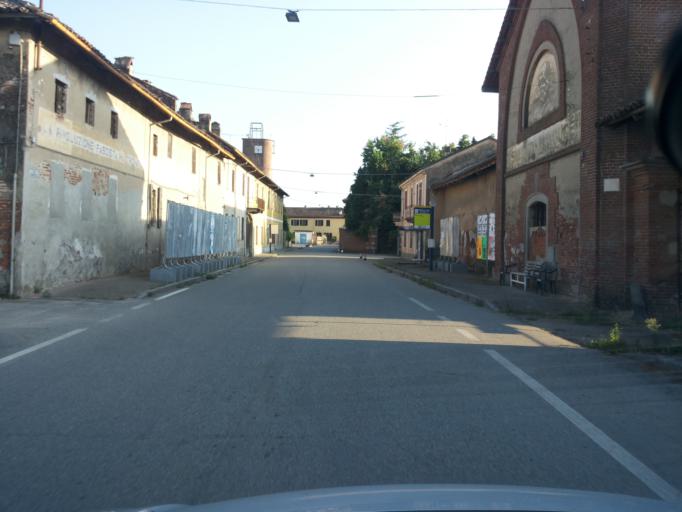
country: IT
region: Piedmont
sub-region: Provincia di Vercelli
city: Sali Vercellese
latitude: 45.3104
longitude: 8.3294
